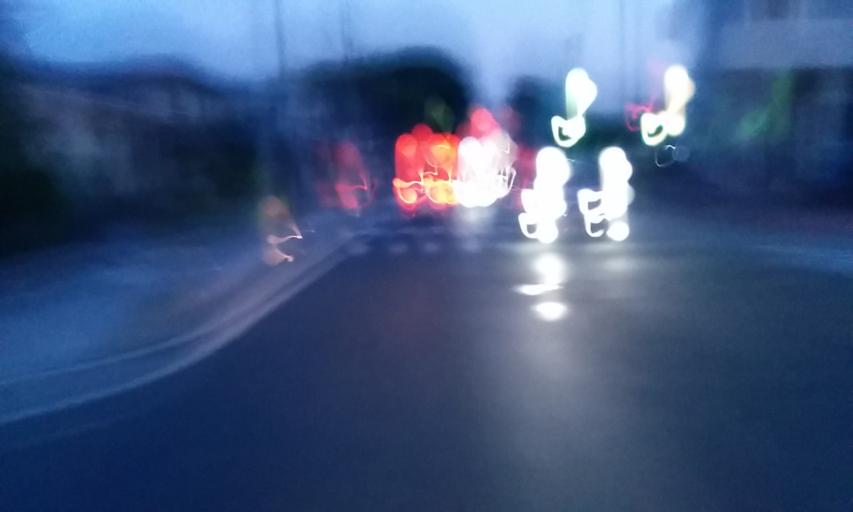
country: JP
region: Ehime
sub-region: Nishiuwa-gun
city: Ikata-cho
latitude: 33.4922
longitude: 132.3974
